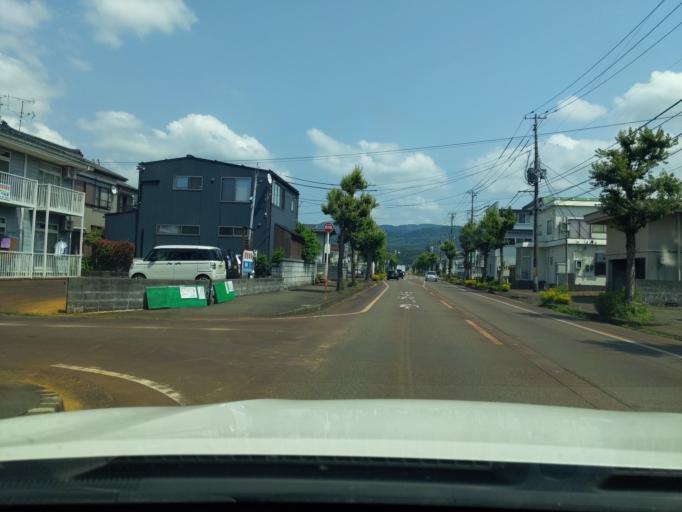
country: JP
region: Niigata
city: Nagaoka
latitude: 37.4299
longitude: 138.8549
